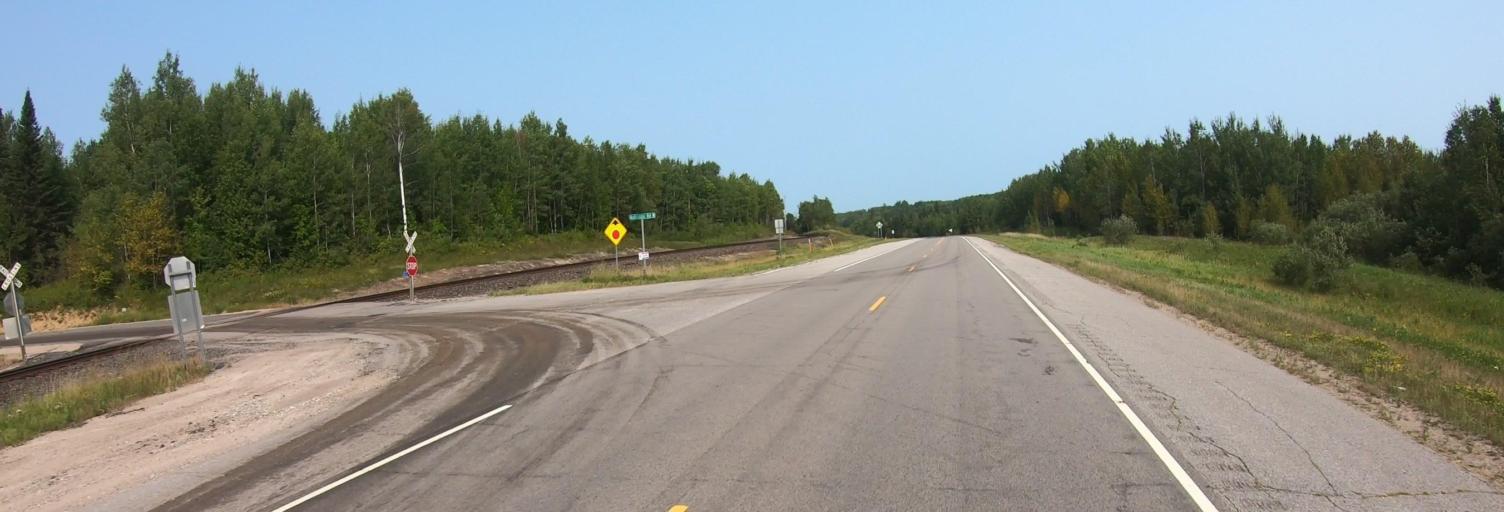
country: CA
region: Ontario
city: Fort Frances
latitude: 48.2332
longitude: -92.9263
